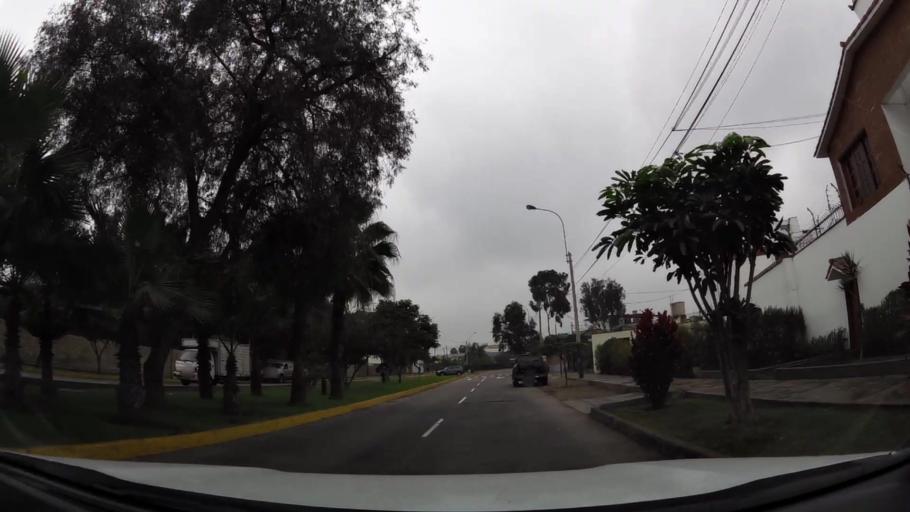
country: PE
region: Lima
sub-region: Lima
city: Surco
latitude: -12.1333
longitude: -77.0000
